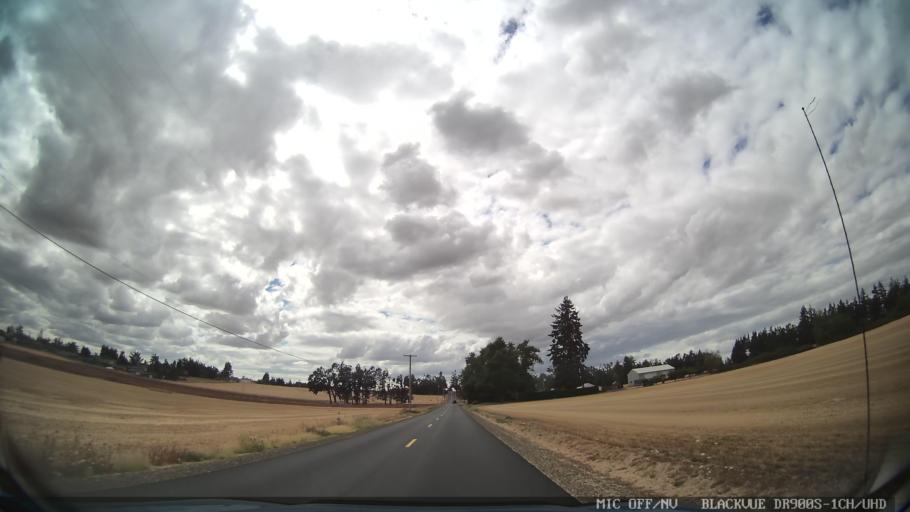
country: US
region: Oregon
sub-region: Marion County
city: Sublimity
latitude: 44.8405
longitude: -122.7808
